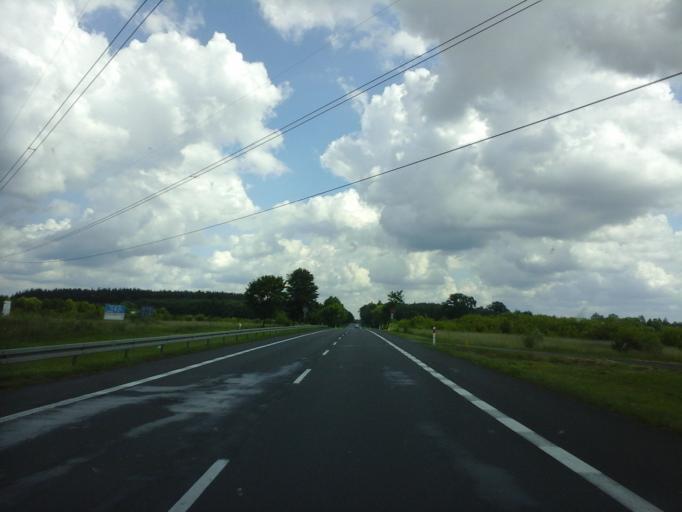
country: PL
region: West Pomeranian Voivodeship
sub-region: Powiat bialogardzki
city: Karlino
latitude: 54.0503
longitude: 15.9073
